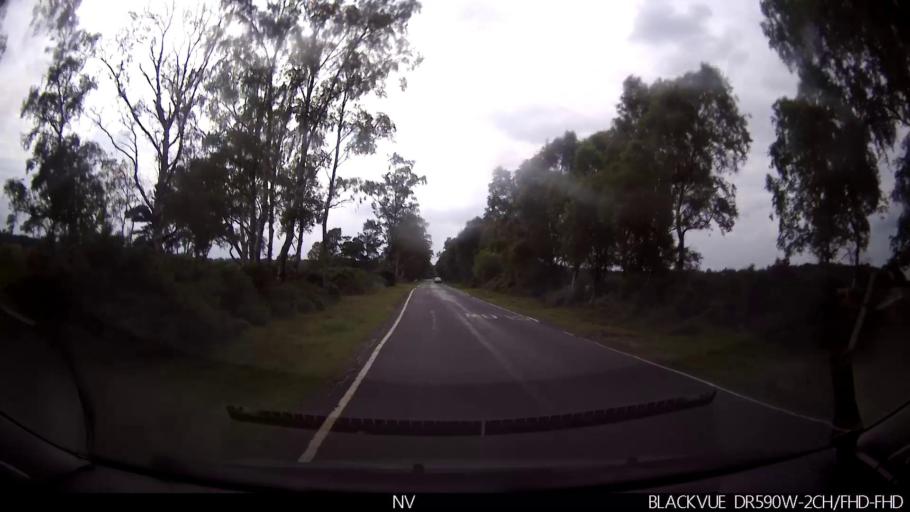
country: GB
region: England
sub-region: North Yorkshire
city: Strensall
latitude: 54.0470
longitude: -0.9968
